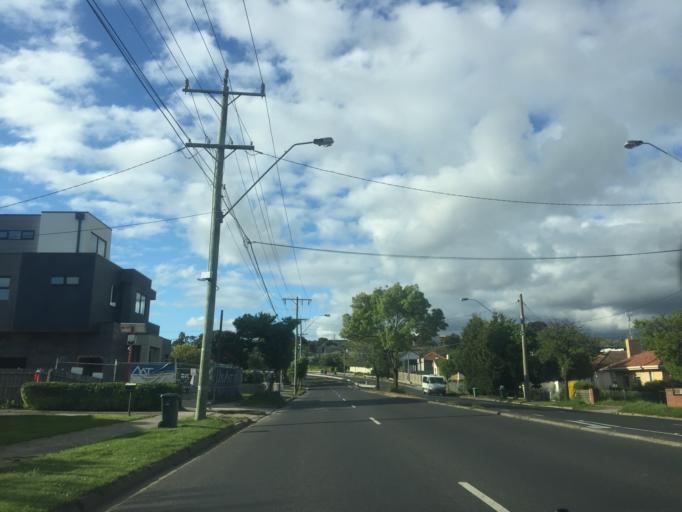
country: AU
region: Victoria
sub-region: Darebin
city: Kingsbury
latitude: -37.7289
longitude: 145.0256
